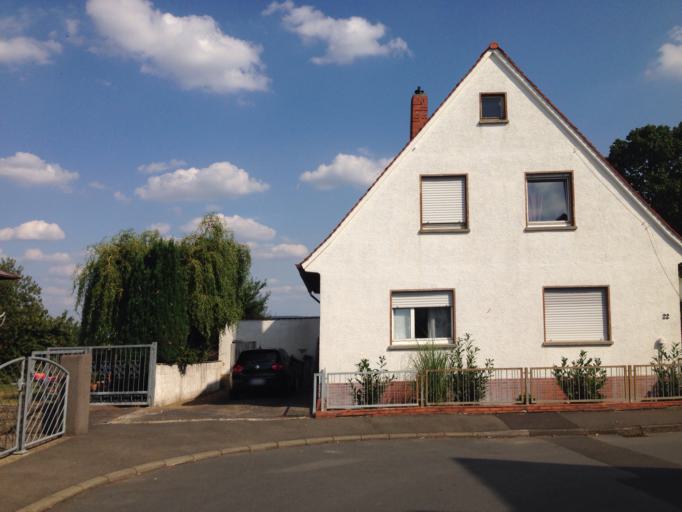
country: DE
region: Hesse
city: Lollar
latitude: 50.6339
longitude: 8.6741
